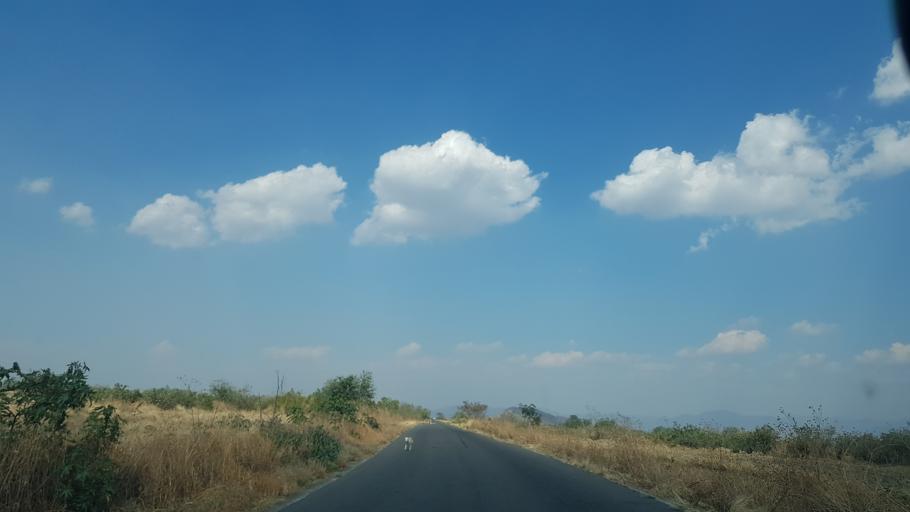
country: MX
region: Puebla
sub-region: Atlixco
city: Colonia Agricola de Ocotepec (Colonia San Jose)
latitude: 18.9179
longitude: -98.5252
